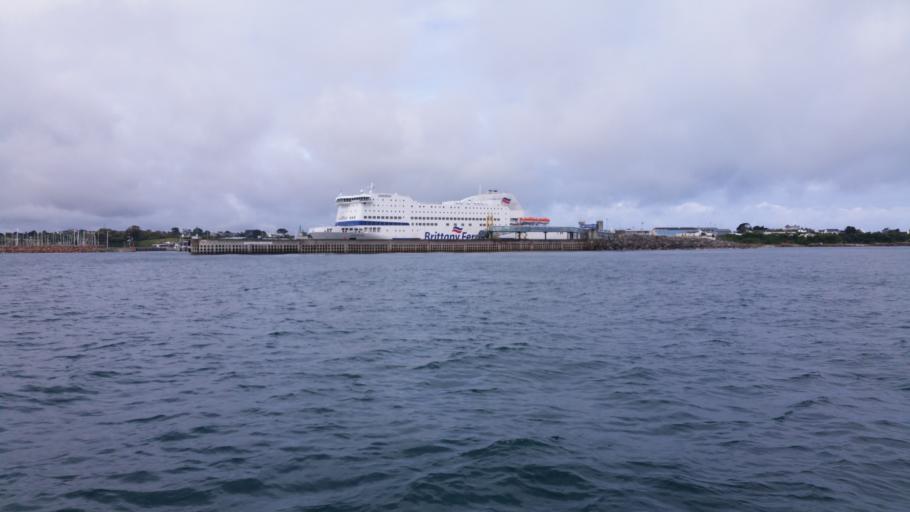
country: FR
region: Brittany
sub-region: Departement du Finistere
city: Roscoff
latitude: 48.7216
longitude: -3.9575
